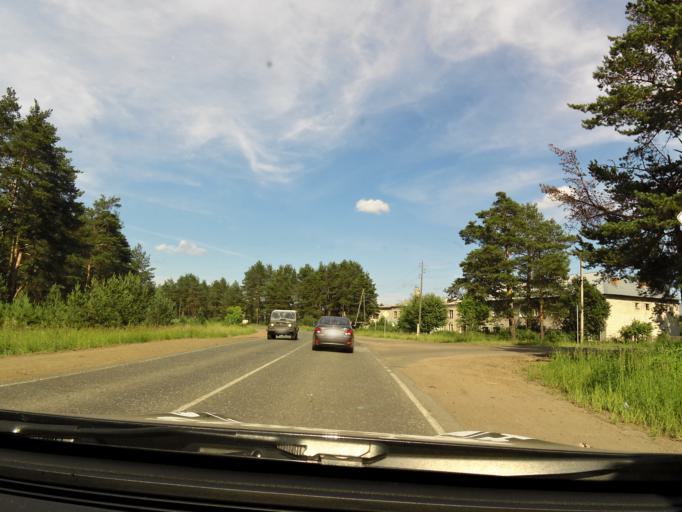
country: RU
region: Kirov
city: Belaya Kholunitsa
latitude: 58.8536
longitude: 50.8362
